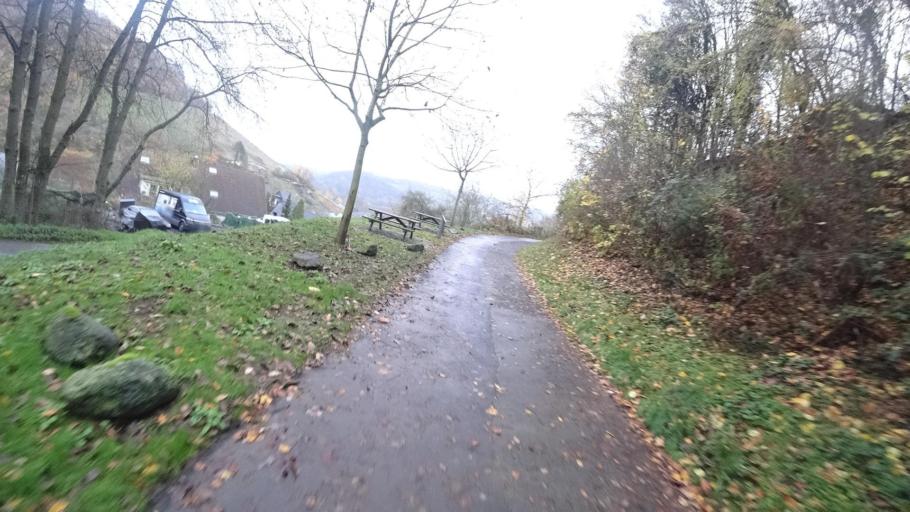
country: DE
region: Rheinland-Pfalz
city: Remagen
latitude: 50.5519
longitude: 7.1843
